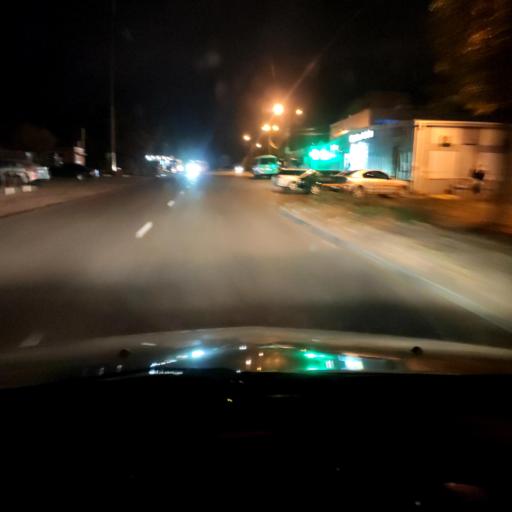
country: RU
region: Voronezj
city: Shilovo
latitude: 51.5517
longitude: 39.0891
